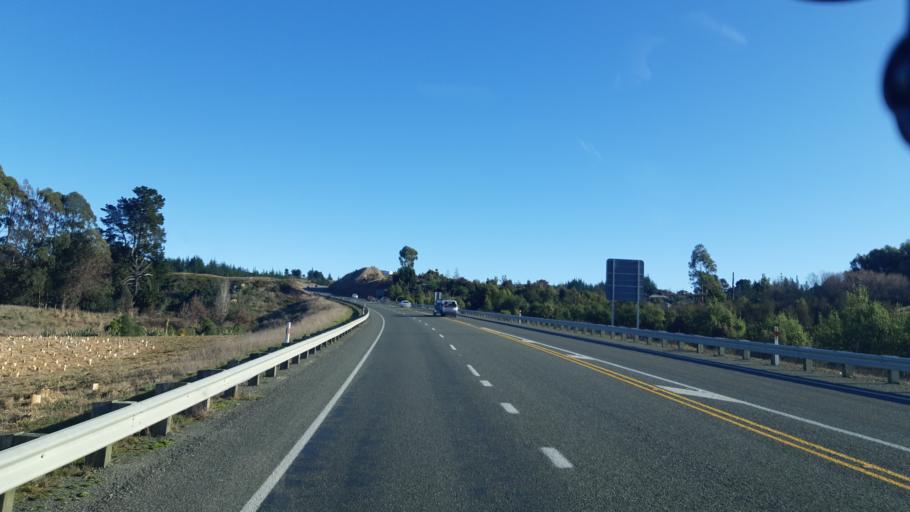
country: NZ
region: Tasman
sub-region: Tasman District
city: Mapua
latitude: -41.2501
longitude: 173.0670
